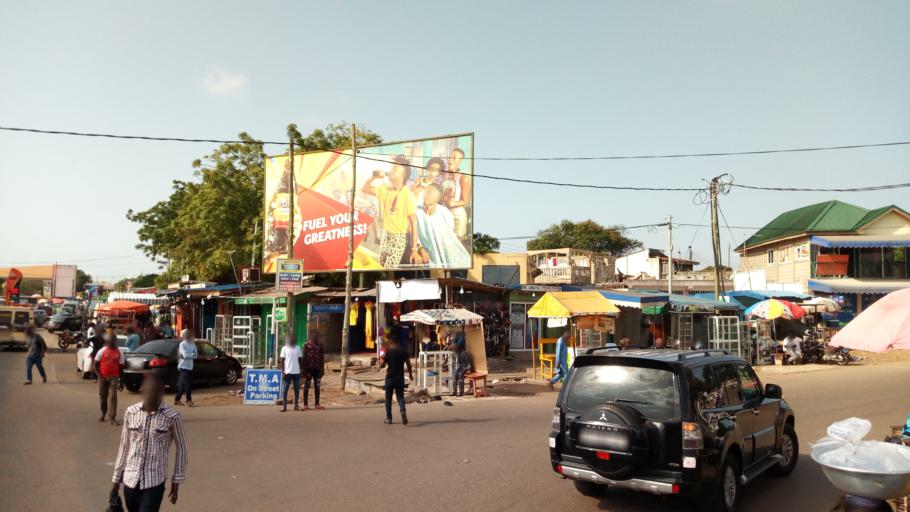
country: GH
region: Greater Accra
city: Tema
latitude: 5.6450
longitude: -0.0007
